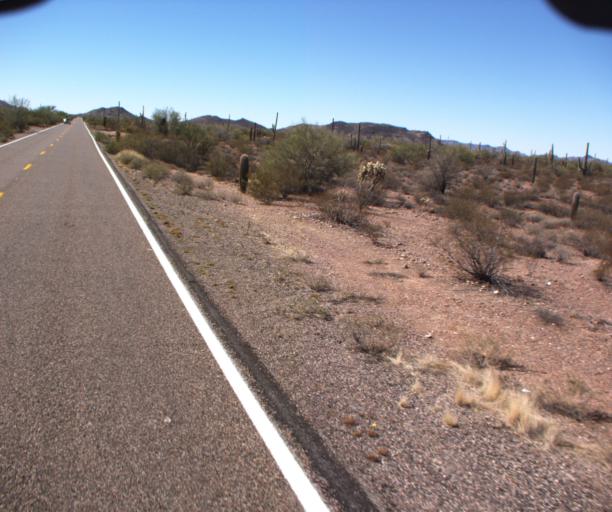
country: MX
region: Sonora
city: Sonoyta
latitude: 32.1154
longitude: -112.7694
